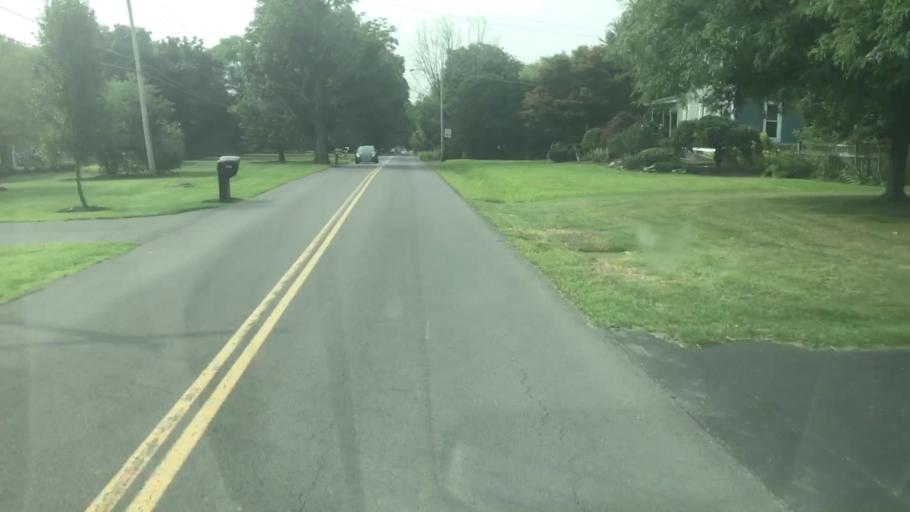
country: US
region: New York
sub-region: Cayuga County
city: Melrose Park
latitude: 42.9170
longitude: -76.5305
